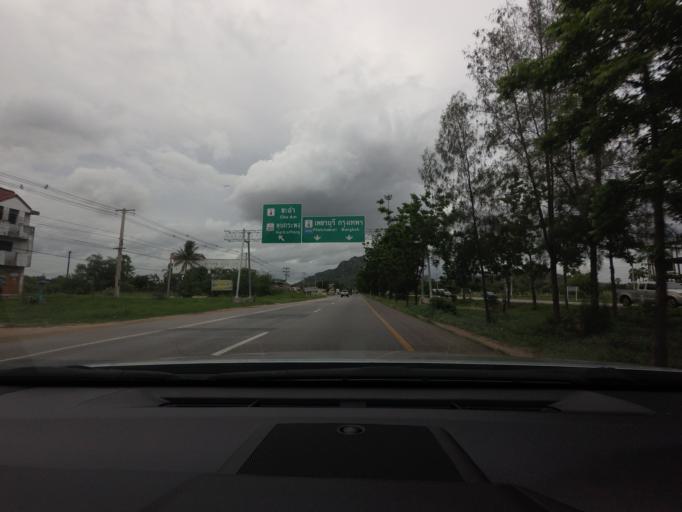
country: TH
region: Phetchaburi
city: Cha-am
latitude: 12.8002
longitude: 99.9417
